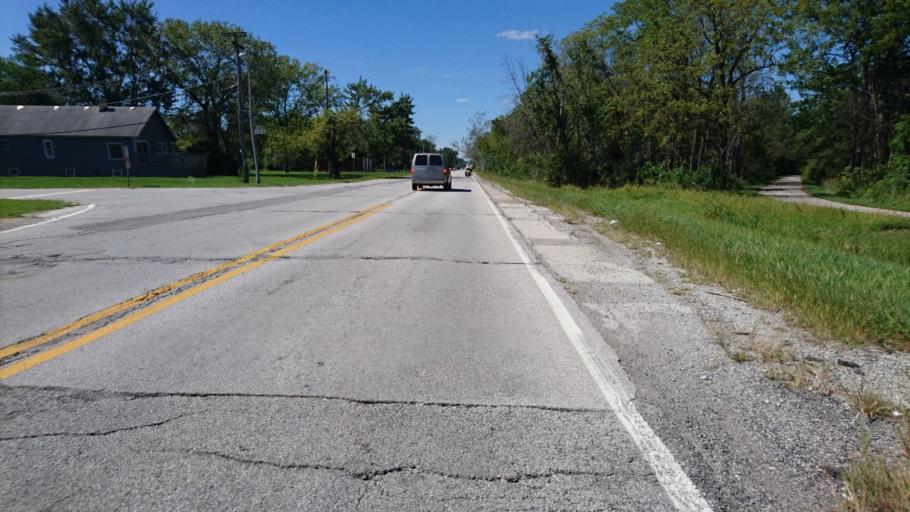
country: US
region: Illinois
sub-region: Cook County
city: Glenwood
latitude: 41.5427
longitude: -87.5850
